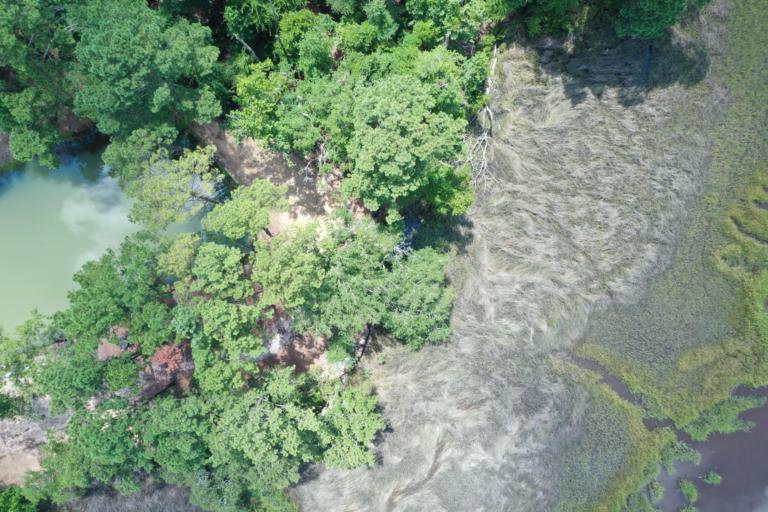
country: US
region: Georgia
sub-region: Chatham County
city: Georgetown
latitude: 32.0271
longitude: -81.2067
